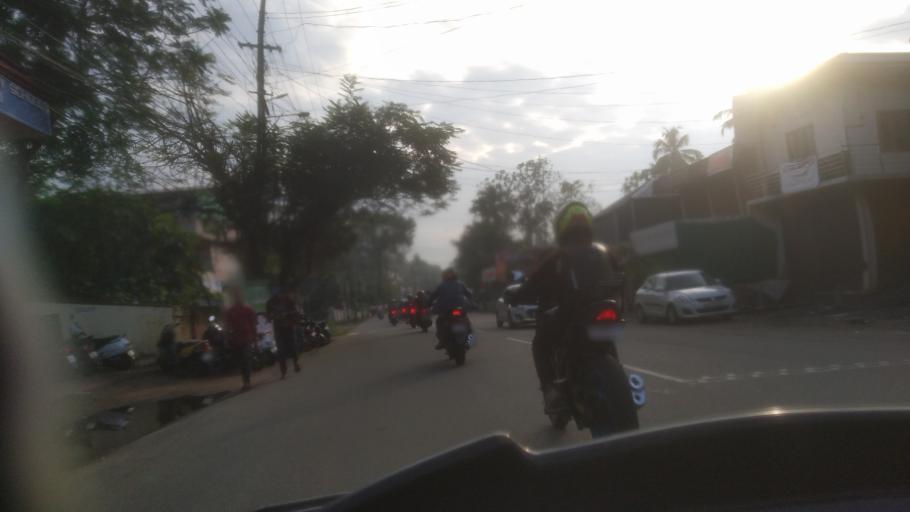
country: IN
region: Kerala
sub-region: Ernakulam
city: Perumpavur
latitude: 10.1168
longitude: 76.4886
